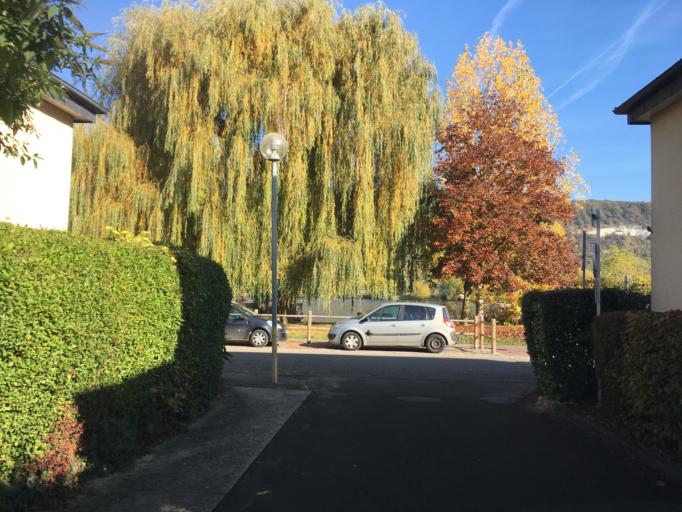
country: FR
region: Haute-Normandie
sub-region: Departement de l'Eure
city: Vernon
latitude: 49.0887
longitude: 1.4959
